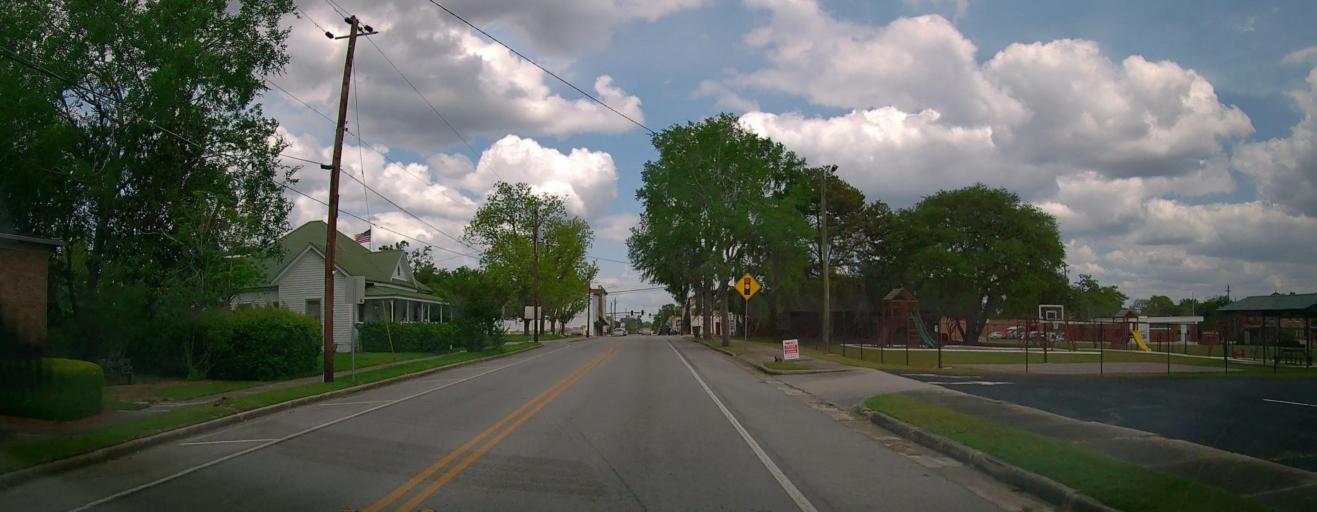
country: US
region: Georgia
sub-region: Treutlen County
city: Soperton
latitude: 32.3761
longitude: -82.5937
